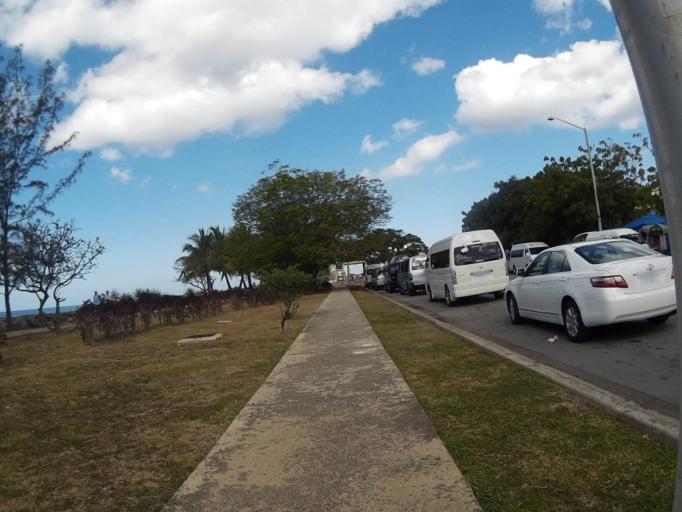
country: BB
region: Saint Michael
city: Bridgetown
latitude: 13.0989
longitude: -59.6254
